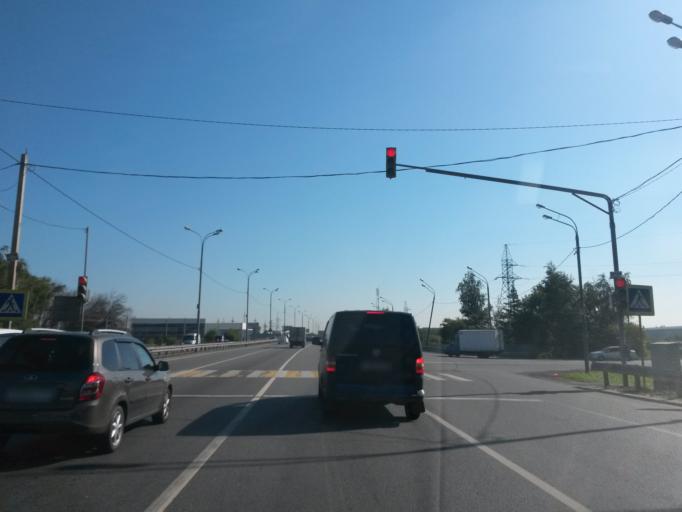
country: RU
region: Moskovskaya
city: Lesnyye Polyany
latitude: 55.9793
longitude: 37.8620
